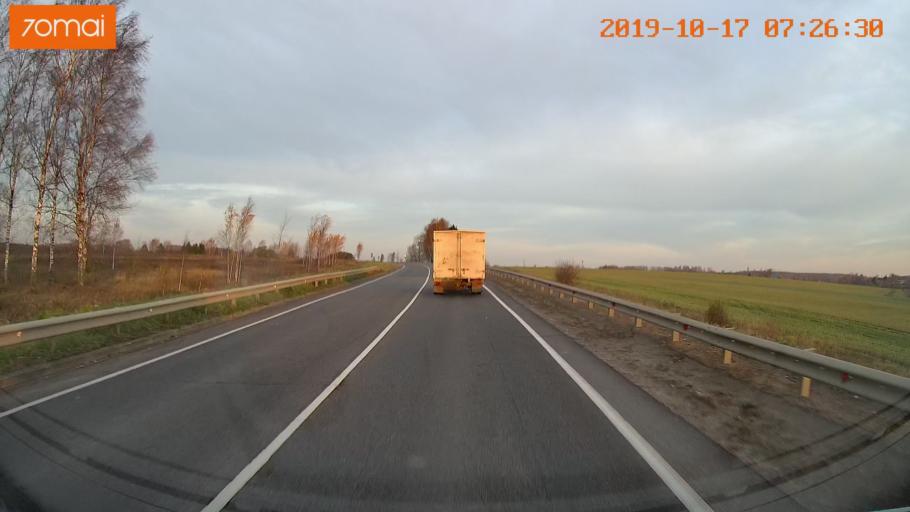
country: RU
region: Ivanovo
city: Gavrilov Posad
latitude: 56.3577
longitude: 40.0920
